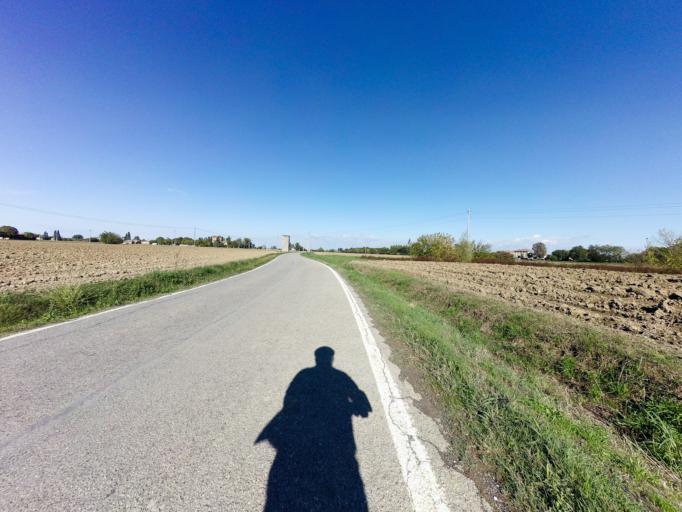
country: IT
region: Emilia-Romagna
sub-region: Provincia di Bologna
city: Progresso
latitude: 44.5591
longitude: 11.3898
